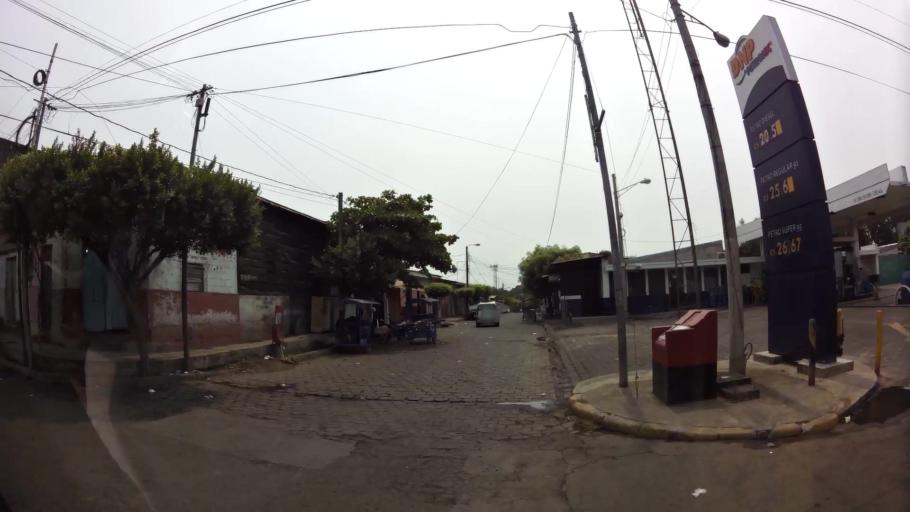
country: NI
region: Chinandega
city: Chinandega
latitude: 12.6328
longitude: -87.1351
